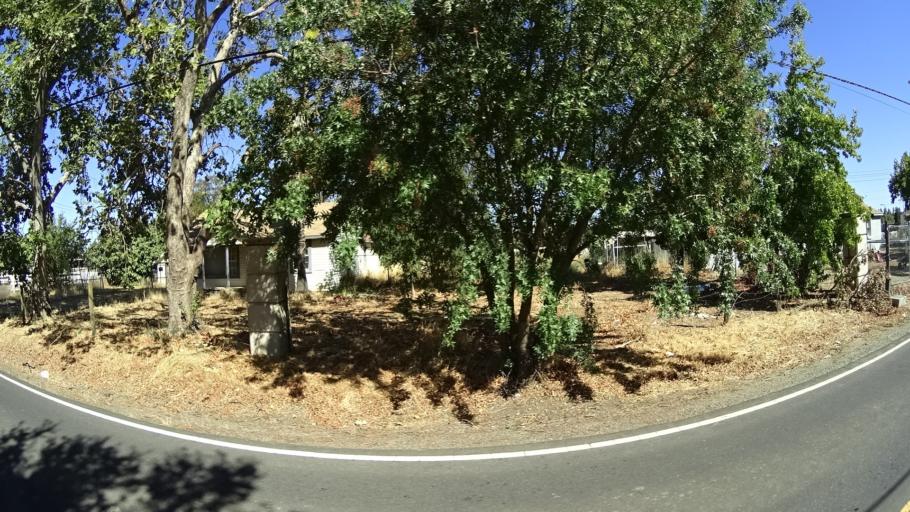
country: US
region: California
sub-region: Sacramento County
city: Wilton
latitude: 38.4237
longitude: -121.3182
